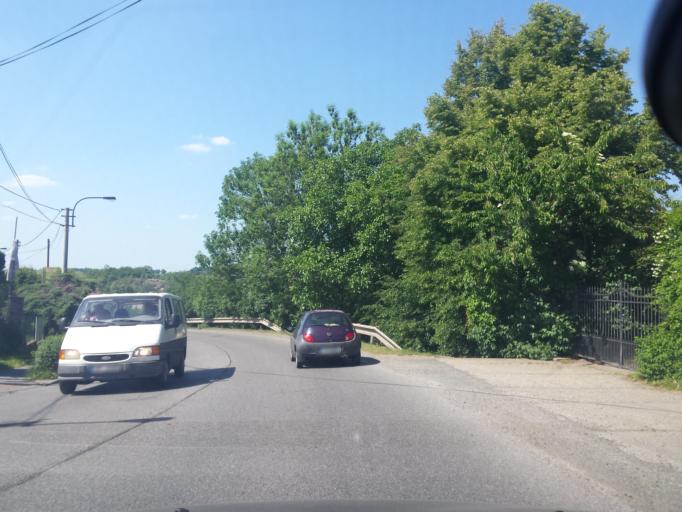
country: CZ
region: Central Bohemia
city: Velke Prilepy
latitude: 50.1571
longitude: 14.3163
